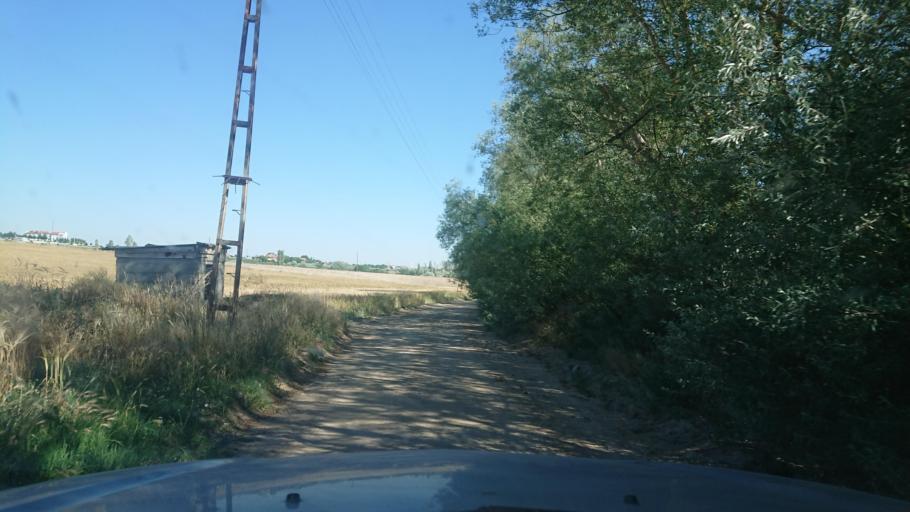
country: TR
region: Aksaray
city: Agacoren
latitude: 38.8579
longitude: 33.9124
